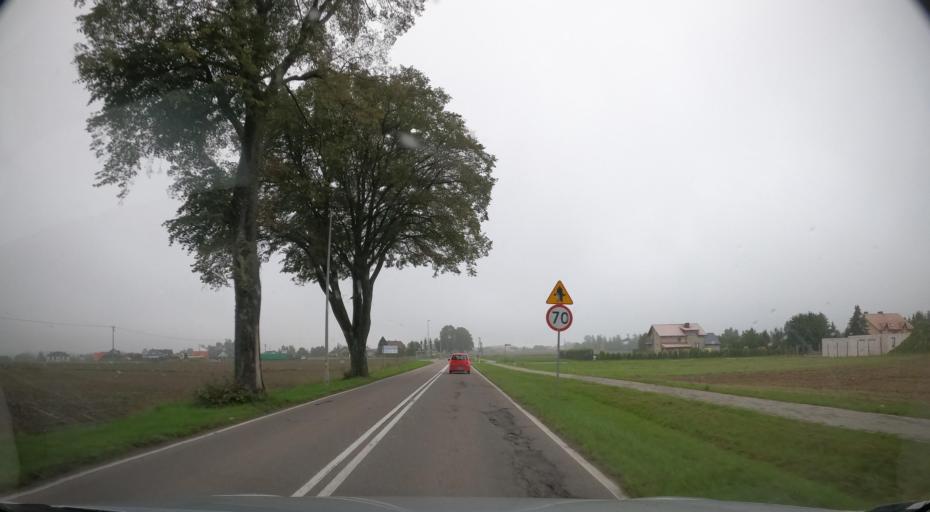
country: PL
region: Pomeranian Voivodeship
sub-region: Powiat wejherowski
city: Bojano
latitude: 54.4524
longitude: 18.3705
